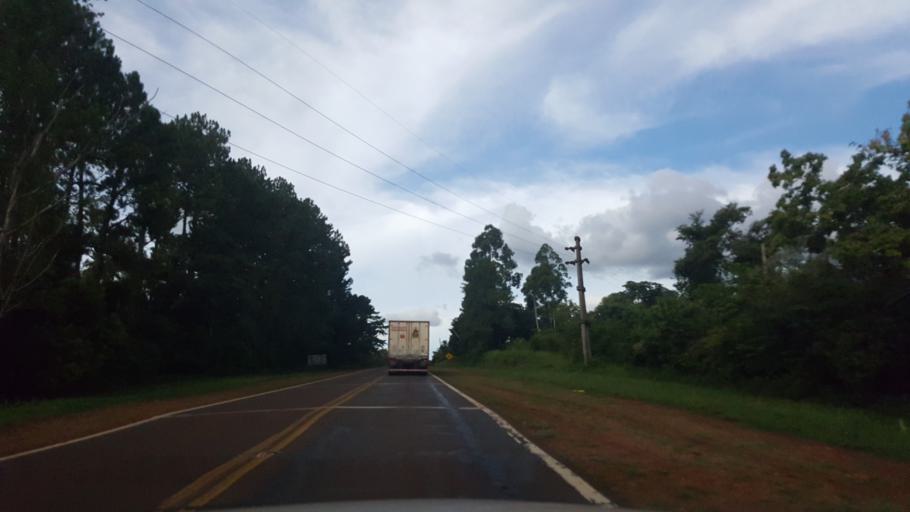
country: AR
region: Misiones
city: Gobernador Roca
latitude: -27.2002
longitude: -55.4797
